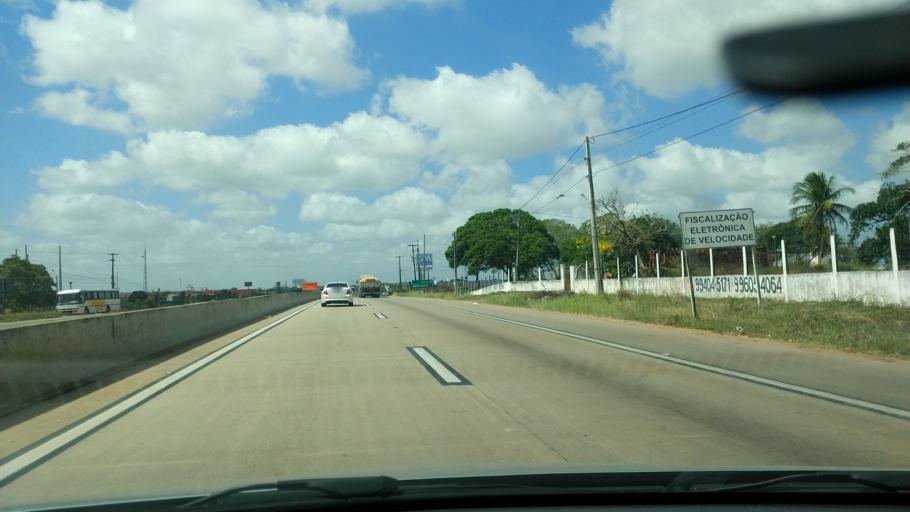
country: BR
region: Rio Grande do Norte
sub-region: Parnamirim
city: Parnamirim
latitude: -5.9446
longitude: -35.2648
